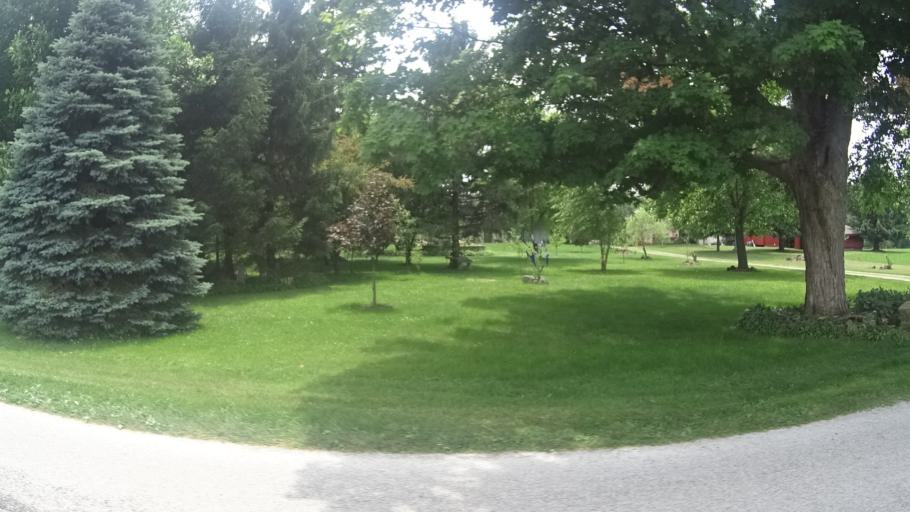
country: US
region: Ohio
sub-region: Erie County
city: Milan
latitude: 41.3100
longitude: -82.6409
